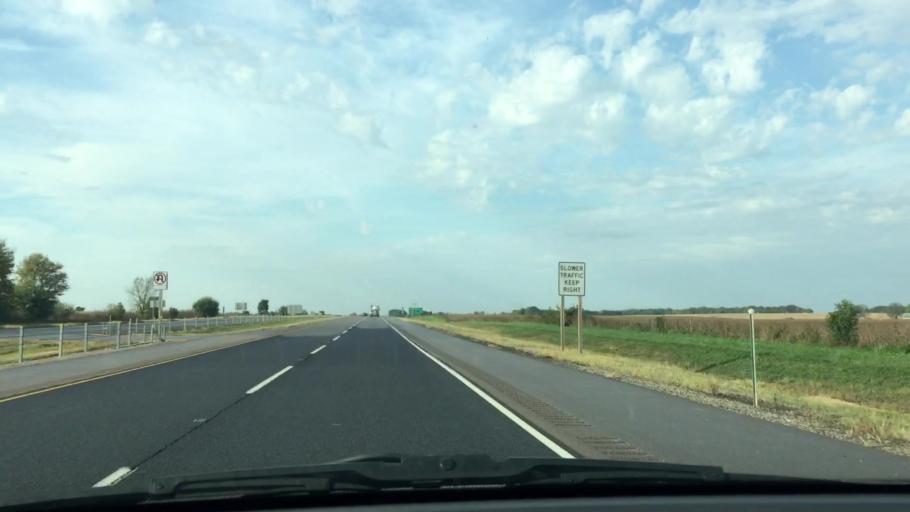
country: US
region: Illinois
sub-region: Lee County
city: Dixon
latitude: 41.8155
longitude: -89.4831
